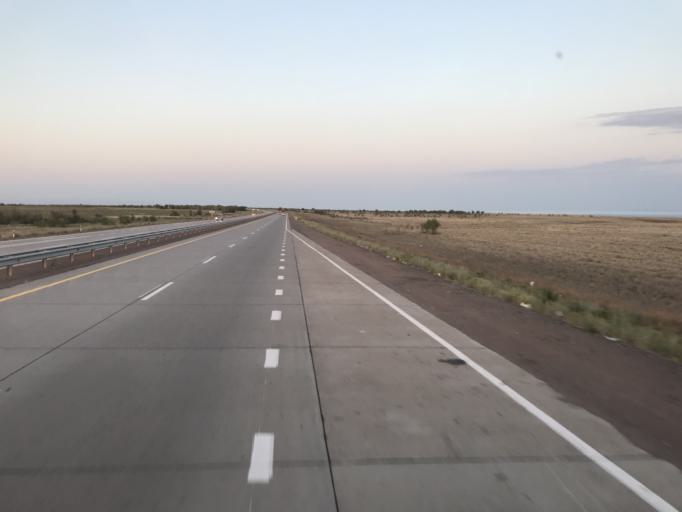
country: KZ
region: Almaty Oblysy
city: Kapshagay
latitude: 43.9236
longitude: 77.1689
